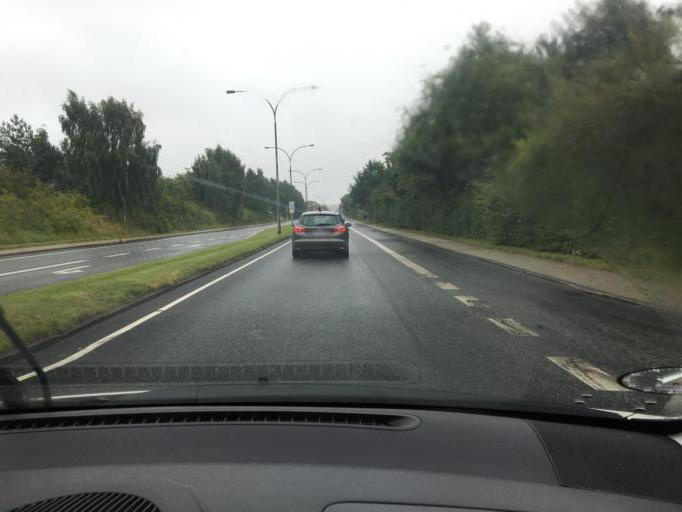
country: DK
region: South Denmark
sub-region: Vejle Kommune
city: Vejle
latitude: 55.6720
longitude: 9.5364
